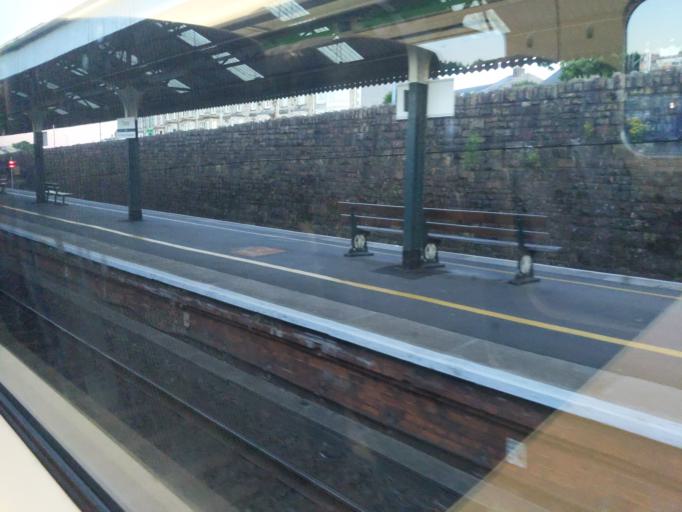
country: GB
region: England
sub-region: Cornwall
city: Truro
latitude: 50.2639
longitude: -5.0657
